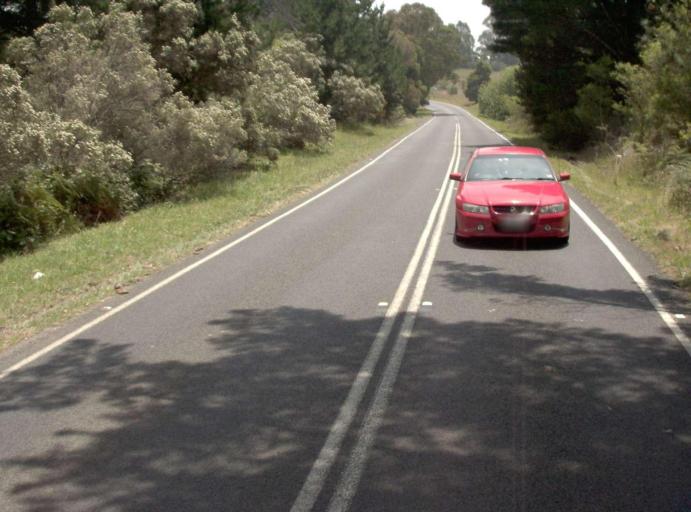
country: AU
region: Victoria
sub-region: Latrobe
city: Traralgon
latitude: -38.3417
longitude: 146.7254
